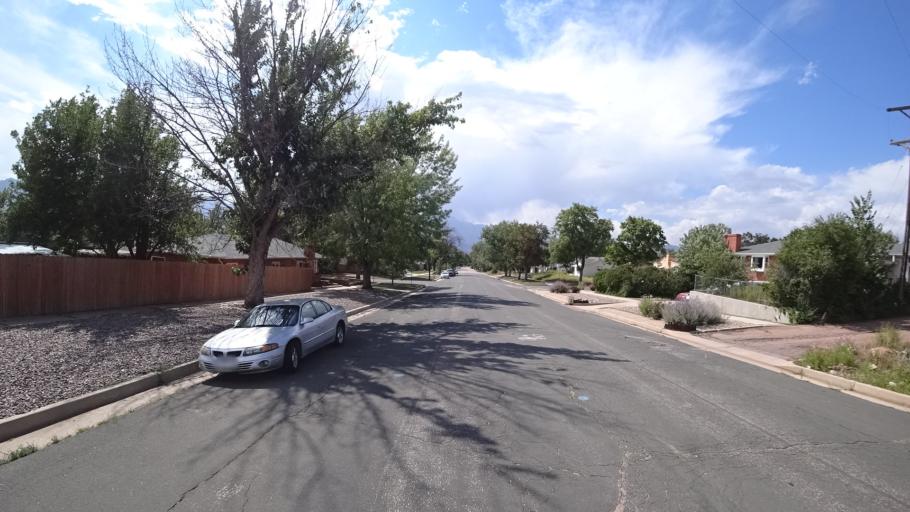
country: US
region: Colorado
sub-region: El Paso County
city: Colorado Springs
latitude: 38.8471
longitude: -104.7995
